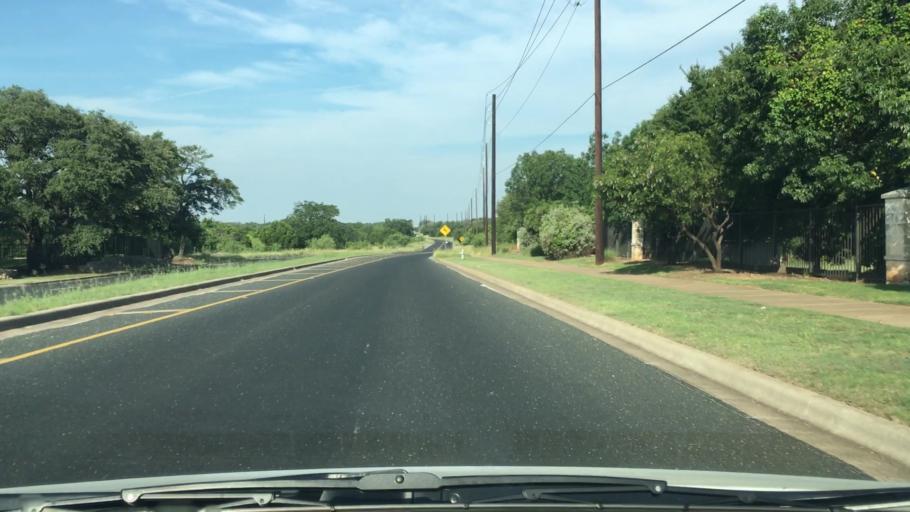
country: US
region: Texas
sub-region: Williamson County
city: Brushy Creek
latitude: 30.4873
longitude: -97.7736
